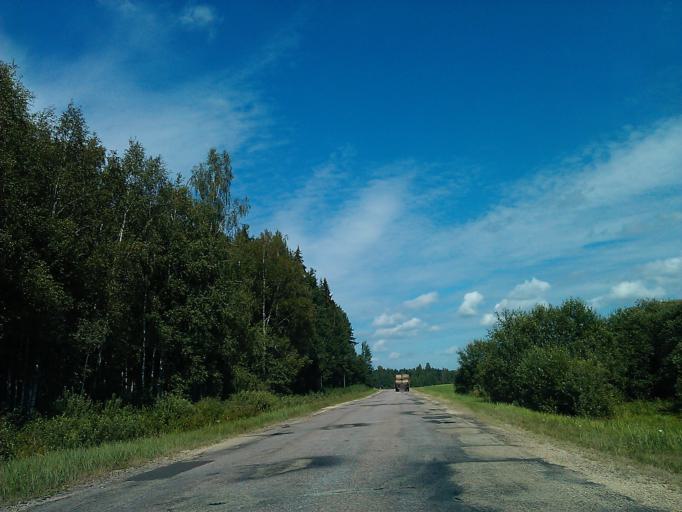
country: LV
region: Ropazu
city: Ropazi
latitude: 56.9283
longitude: 24.6248
